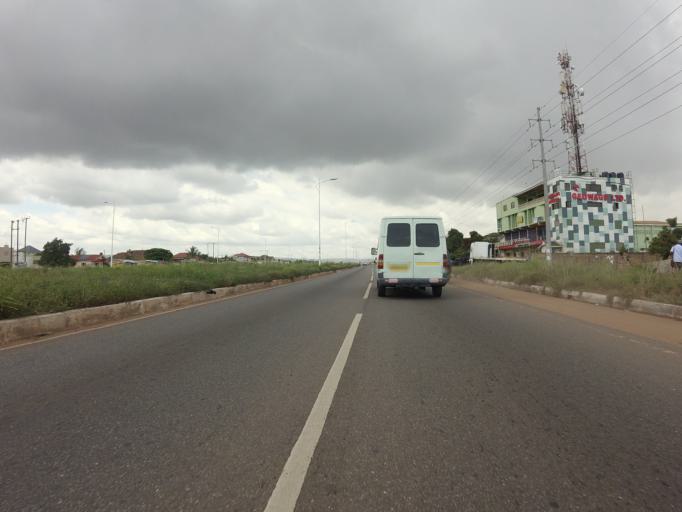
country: GH
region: Greater Accra
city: Medina Estates
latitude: 5.7105
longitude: -0.1712
